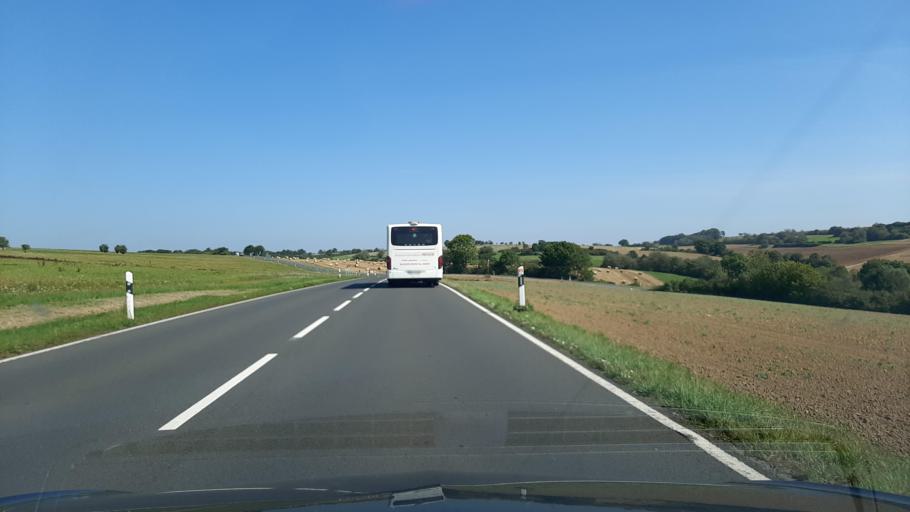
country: DE
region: Rheinland-Pfalz
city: Metterich
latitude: 49.9722
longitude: 6.5913
